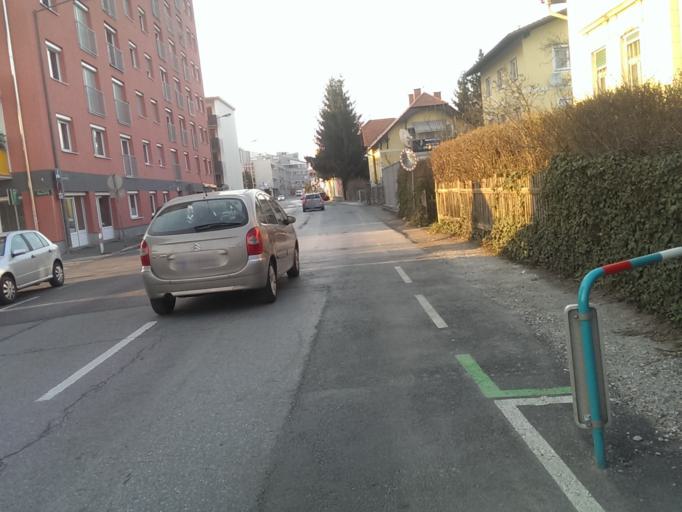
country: AT
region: Styria
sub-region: Graz Stadt
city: Graz
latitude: 47.0445
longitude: 15.4576
